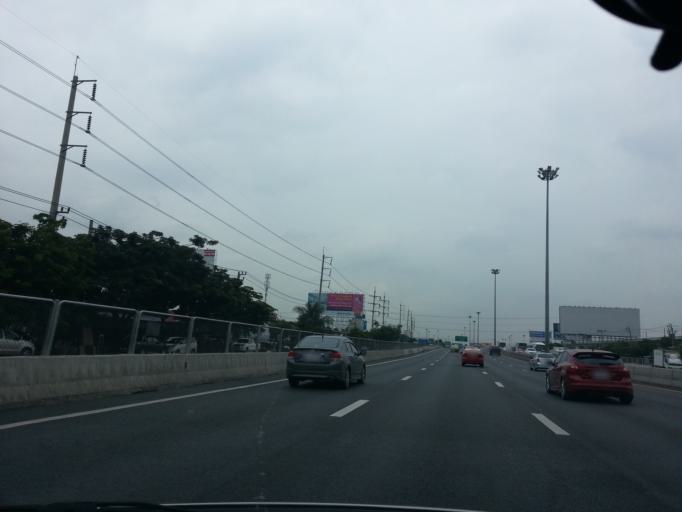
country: TH
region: Bangkok
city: Saphan Sung
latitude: 13.7338
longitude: 100.6927
